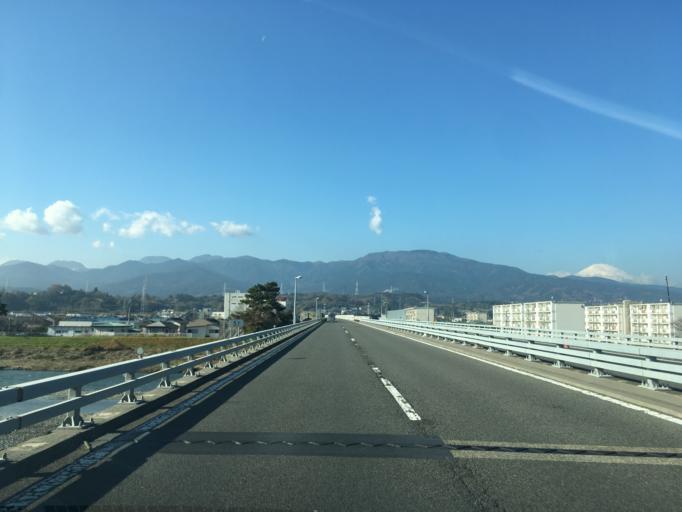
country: JP
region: Kanagawa
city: Odawara
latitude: 35.2836
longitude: 139.1599
